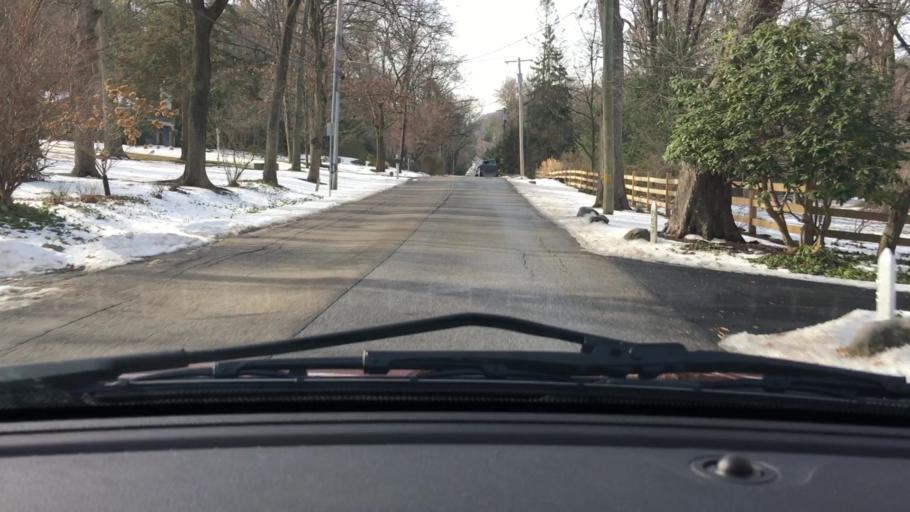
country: US
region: Pennsylvania
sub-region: Montgomery County
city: Flourtown
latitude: 40.0834
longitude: -75.2367
